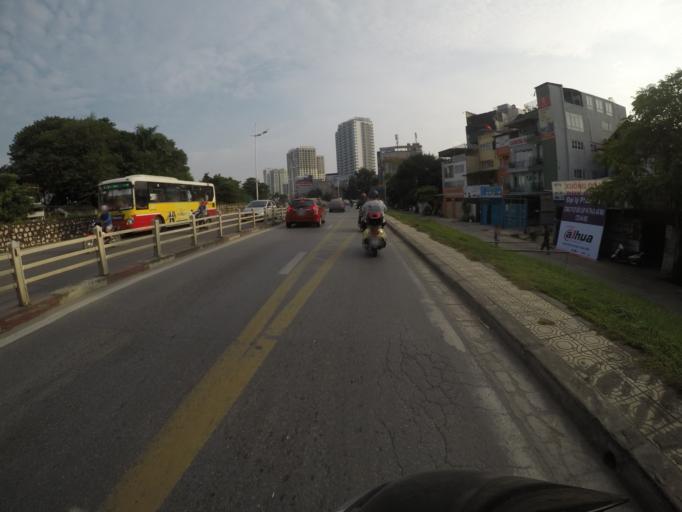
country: VN
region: Ha Noi
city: Tay Ho
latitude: 21.0697
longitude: 105.8261
